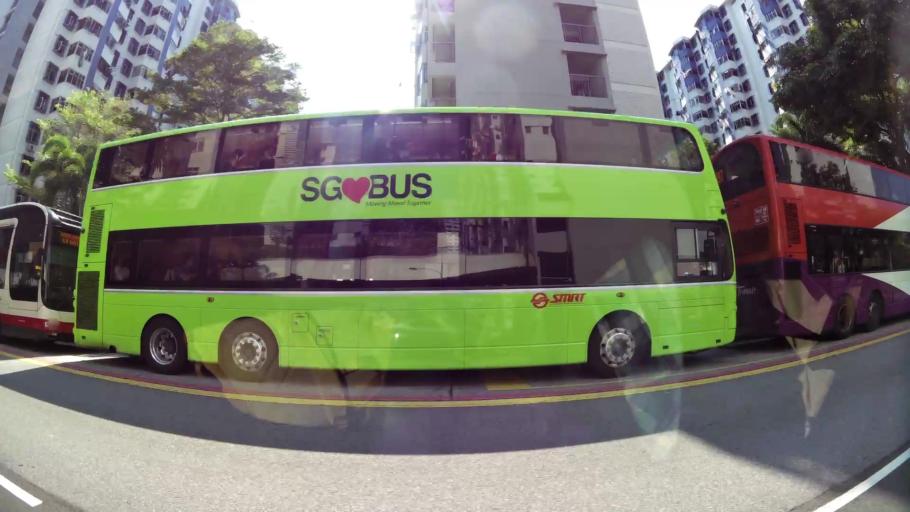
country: SG
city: Singapore
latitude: 1.3050
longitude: 103.8637
